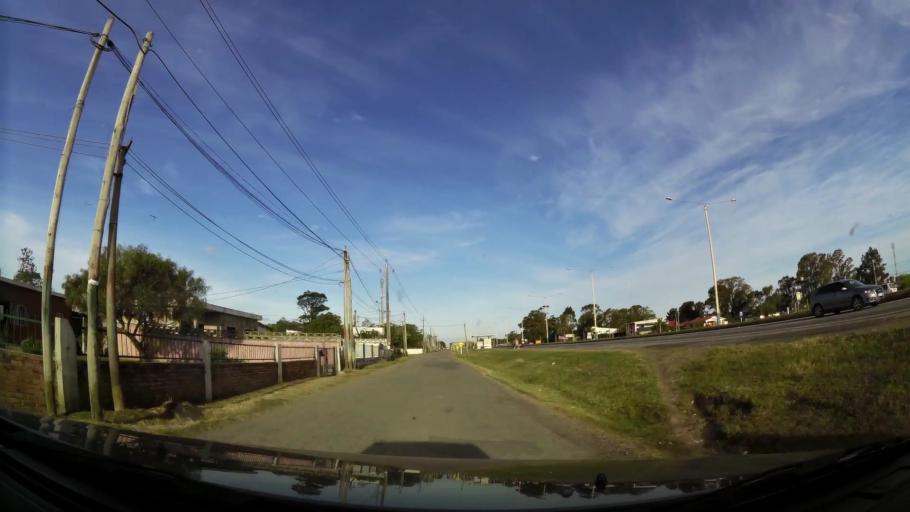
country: UY
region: Canelones
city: Atlantida
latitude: -34.7757
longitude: -55.8454
